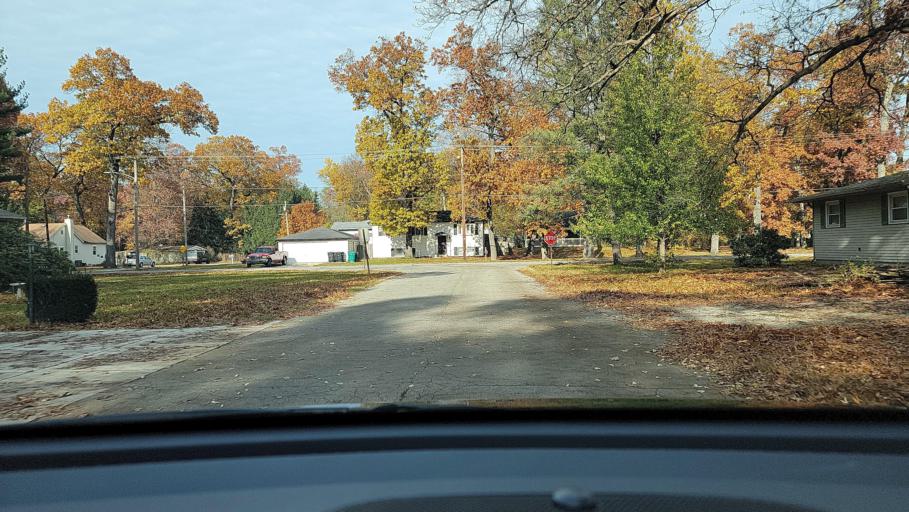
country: US
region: Indiana
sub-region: Porter County
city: Portage
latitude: 41.5791
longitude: -87.1948
